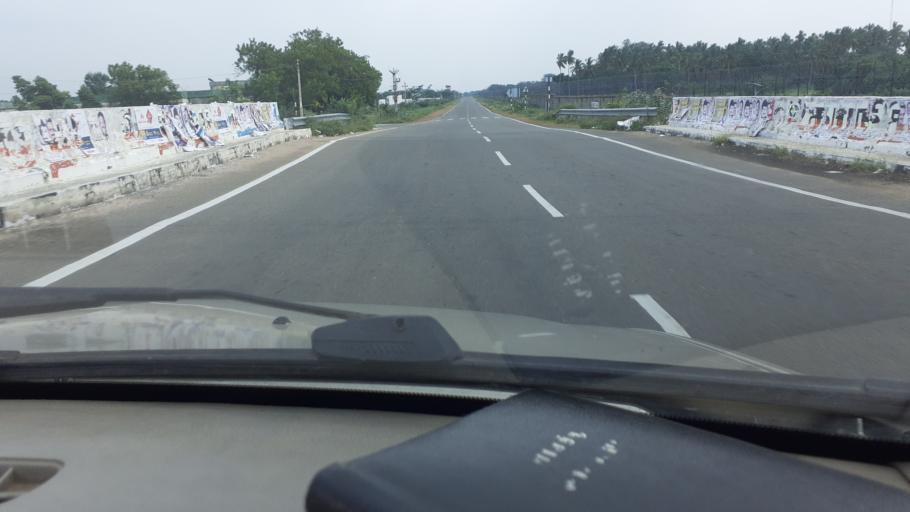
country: IN
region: Tamil Nadu
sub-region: Tirunelveli Kattabo
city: Nanguneri
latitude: 8.4063
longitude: 77.7558
